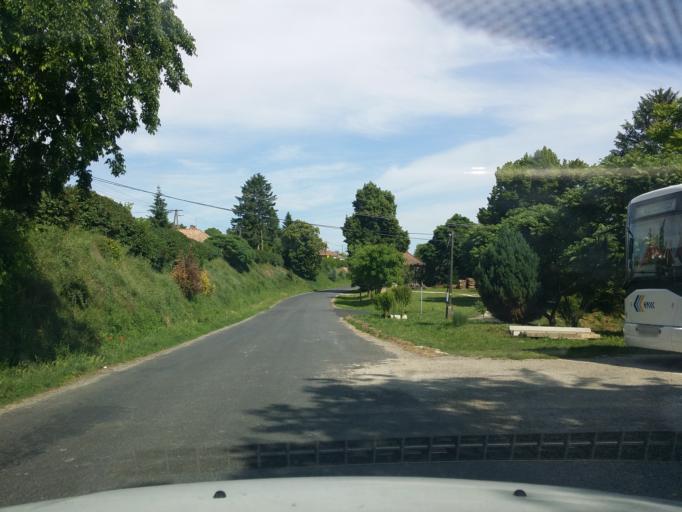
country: HU
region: Zala
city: Zalaszentgrot
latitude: 46.8868
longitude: 17.0718
